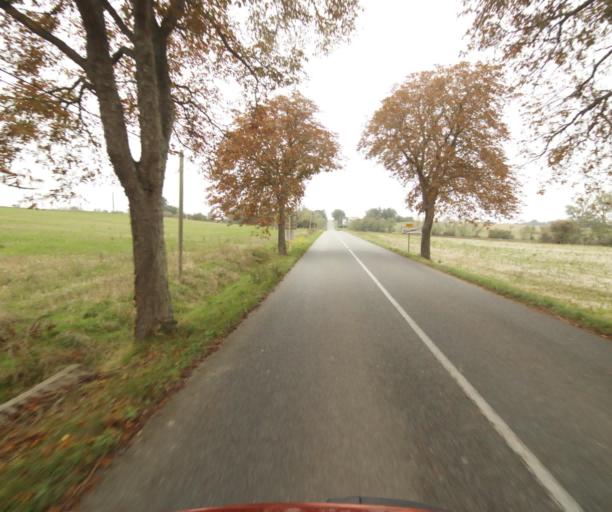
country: FR
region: Midi-Pyrenees
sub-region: Departement du Tarn-et-Garonne
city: Verdun-sur-Garonne
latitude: 43.8060
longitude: 1.2094
